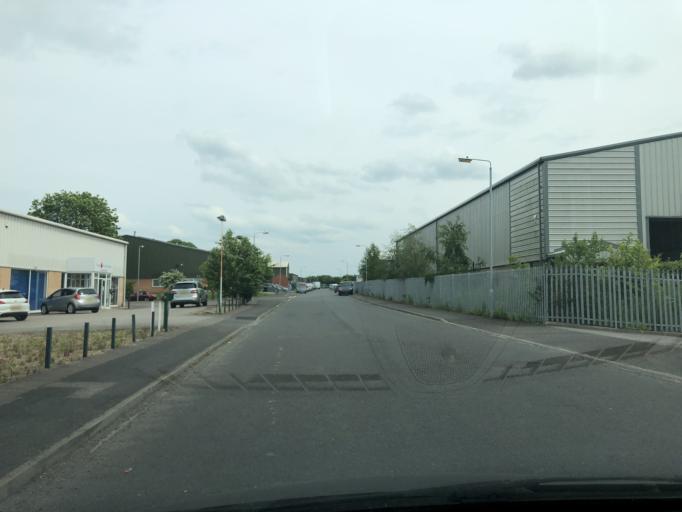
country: GB
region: England
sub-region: North Yorkshire
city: Pickering
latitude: 54.2370
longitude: -0.7612
